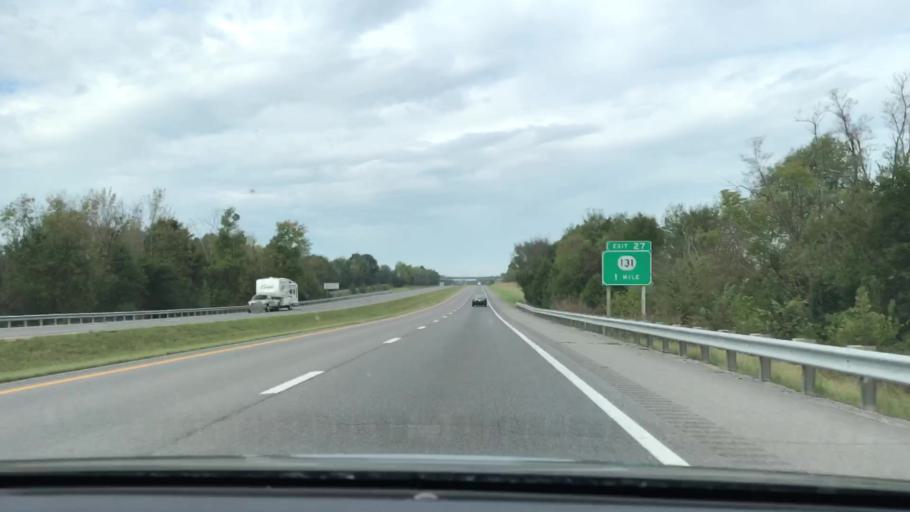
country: US
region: Kentucky
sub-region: Graves County
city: Mayfield
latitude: 36.7789
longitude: -88.5743
